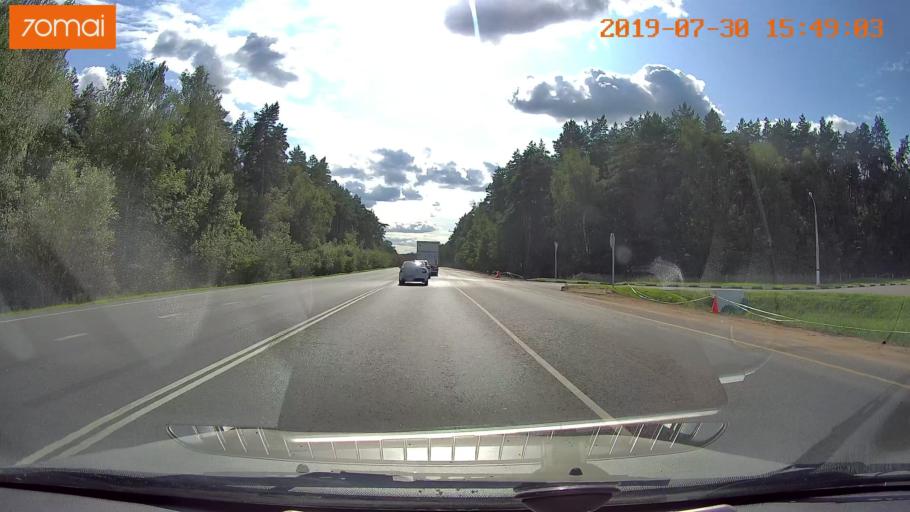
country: RU
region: Moskovskaya
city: Voskresensk
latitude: 55.3395
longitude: 38.6733
